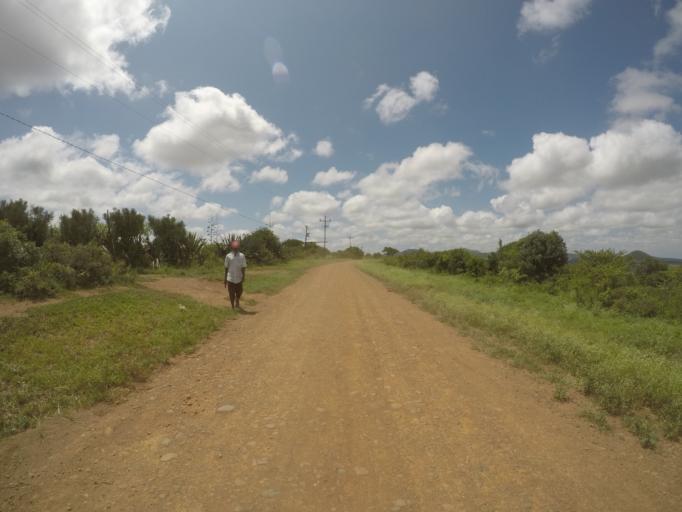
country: ZA
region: KwaZulu-Natal
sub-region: uThungulu District Municipality
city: Empangeni
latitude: -28.5860
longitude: 31.8234
